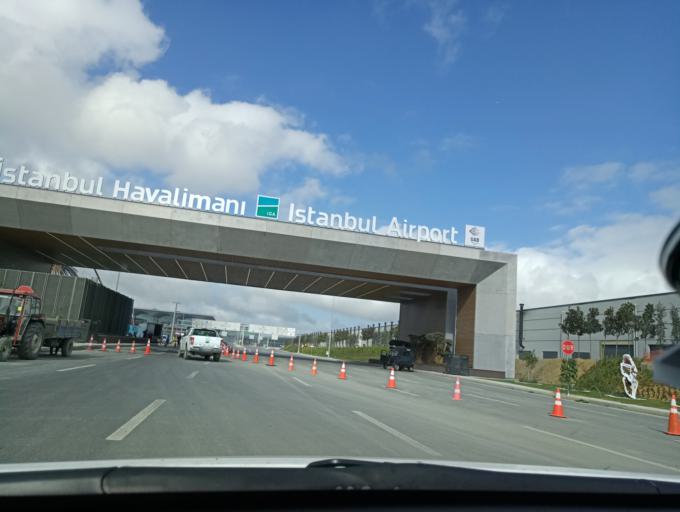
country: TR
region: Istanbul
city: Durusu
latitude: 41.2513
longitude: 28.7466
